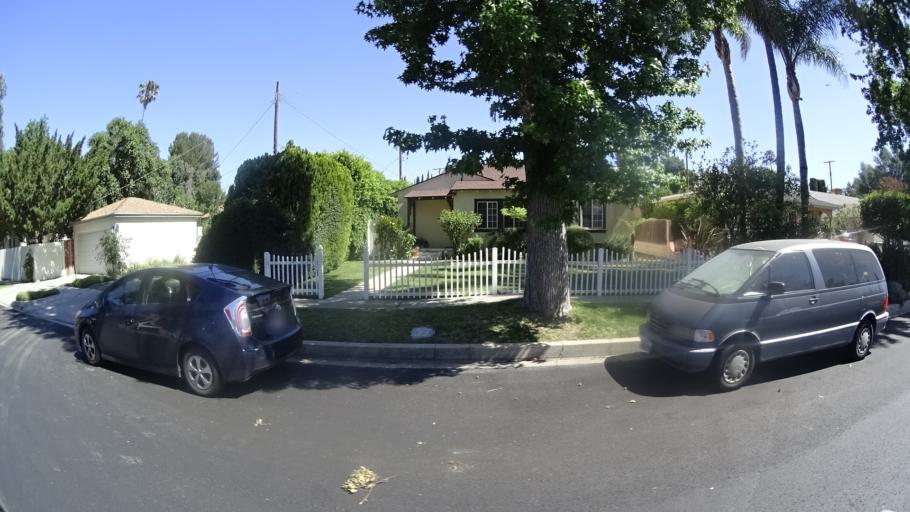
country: US
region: California
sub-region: Los Angeles County
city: Van Nuys
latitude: 34.1875
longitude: -118.4918
